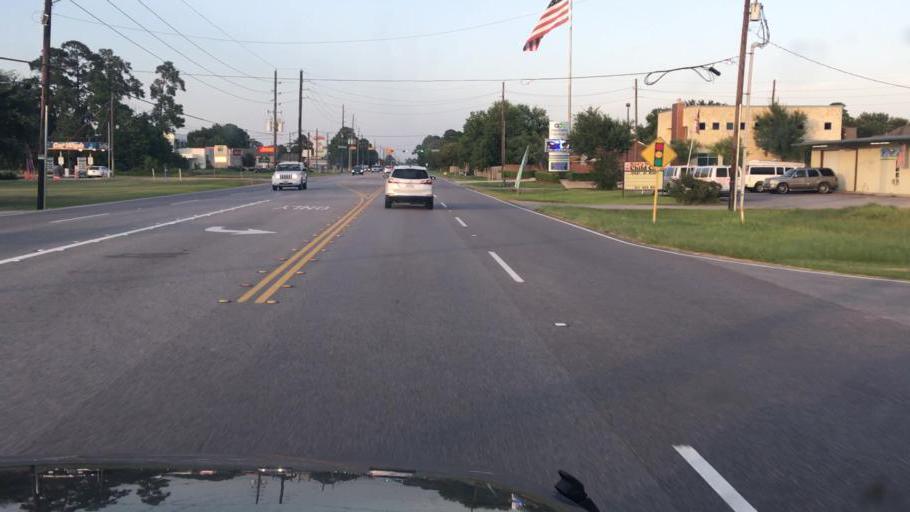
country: US
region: Texas
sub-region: Harris County
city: Atascocita
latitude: 29.9940
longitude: -95.1760
